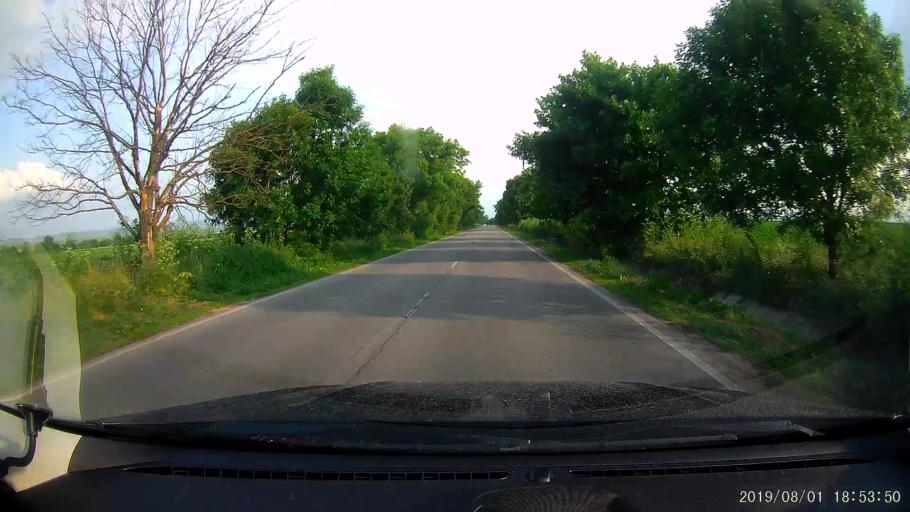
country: BG
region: Shumen
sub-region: Obshtina Shumen
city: Shumen
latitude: 43.2137
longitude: 26.9979
